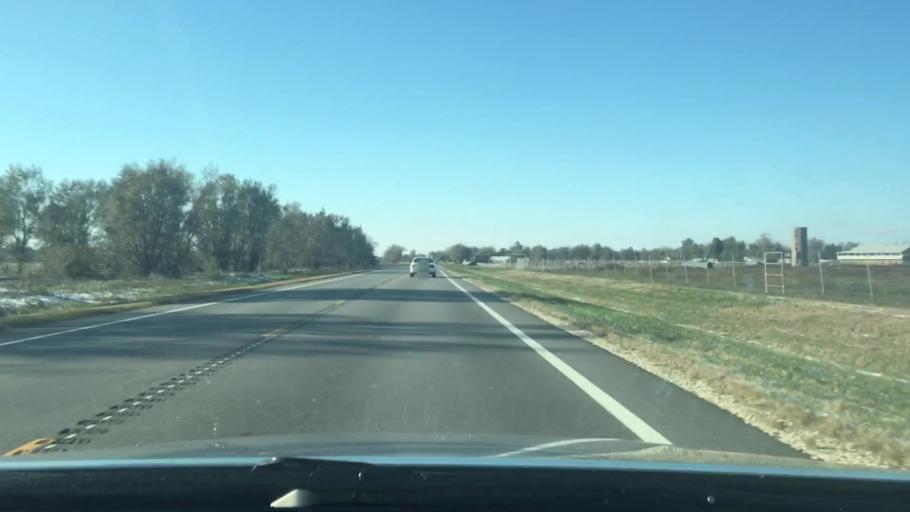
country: US
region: Kansas
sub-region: Reno County
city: Nickerson
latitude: 38.1384
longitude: -98.0705
